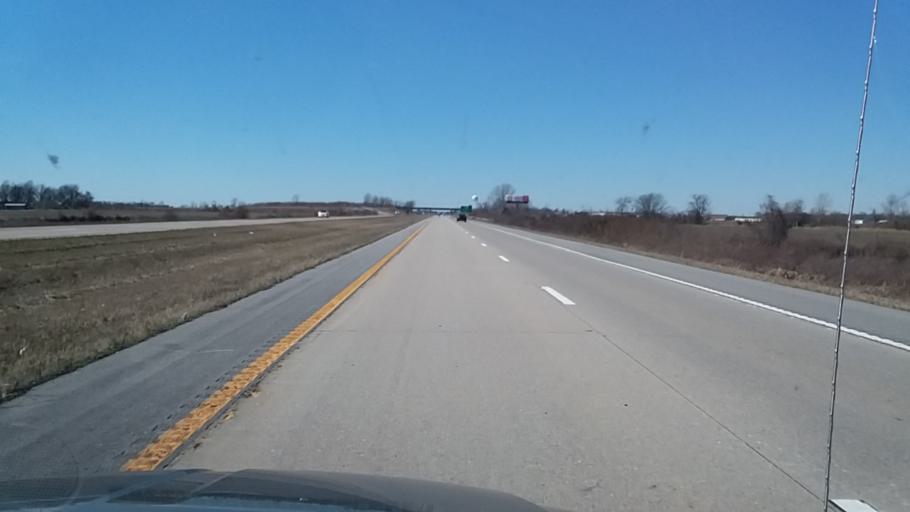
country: US
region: Missouri
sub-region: Pemiscot County
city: Caruthersville
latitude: 36.1476
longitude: -89.6543
